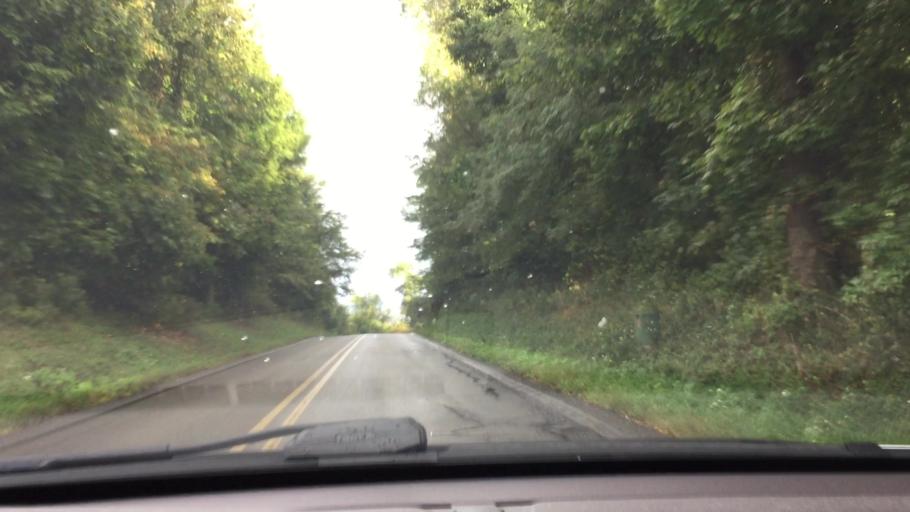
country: US
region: Pennsylvania
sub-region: Washington County
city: McGovern
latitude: 40.2192
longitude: -80.1886
